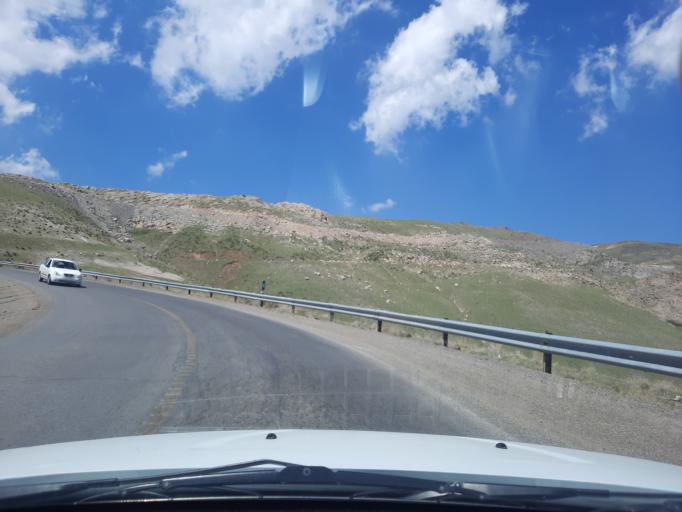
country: IR
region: Qazvin
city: Qazvin
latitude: 36.3687
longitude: 50.2049
